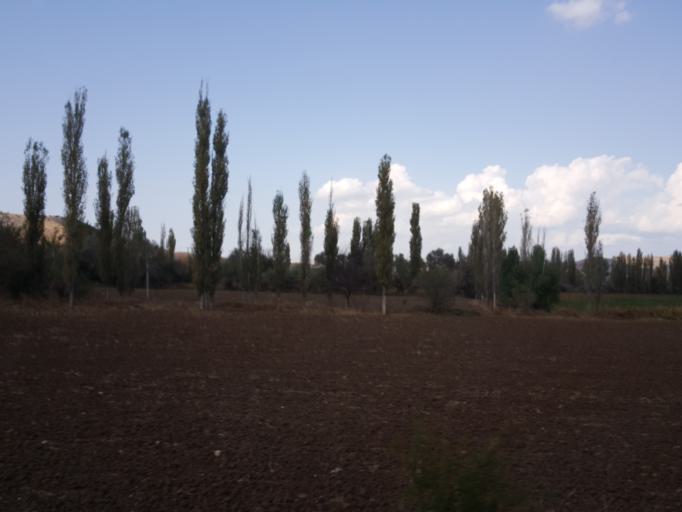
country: TR
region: Corum
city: Bogazkale
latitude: 40.1274
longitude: 34.5337
